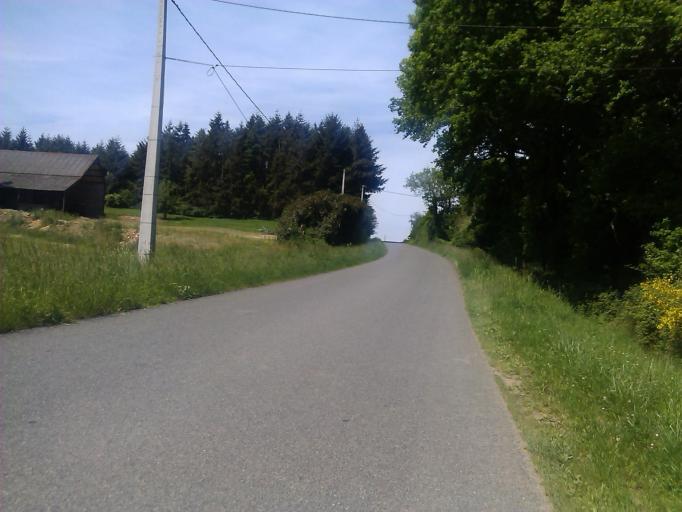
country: FR
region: Centre
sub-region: Departement du Cher
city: Le Chatelet
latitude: 46.5819
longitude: 2.3828
